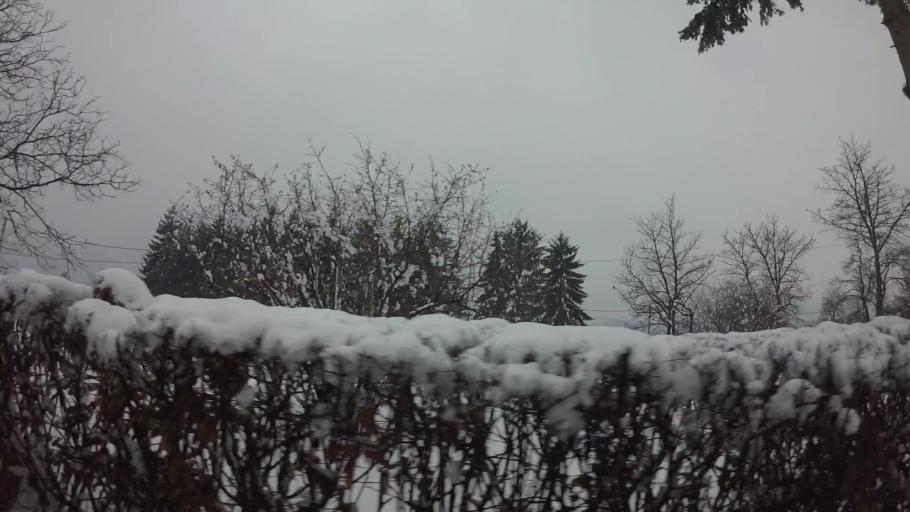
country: BA
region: Federation of Bosnia and Herzegovina
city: Hadzici
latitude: 43.8503
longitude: 18.2591
